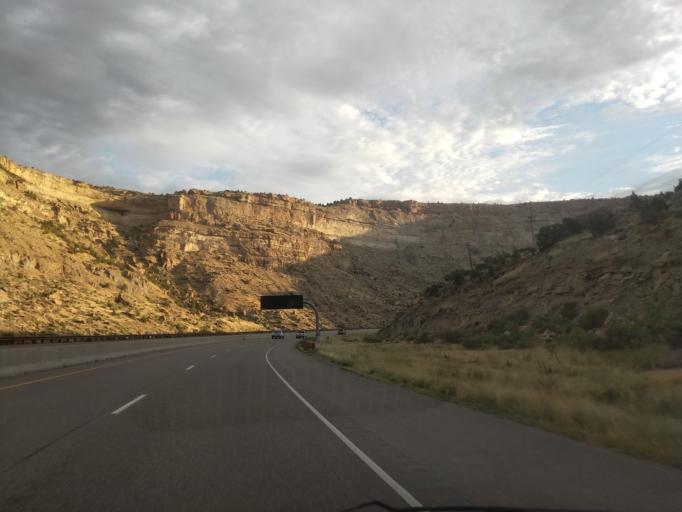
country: US
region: Colorado
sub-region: Mesa County
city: Palisade
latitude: 39.1914
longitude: -108.2814
